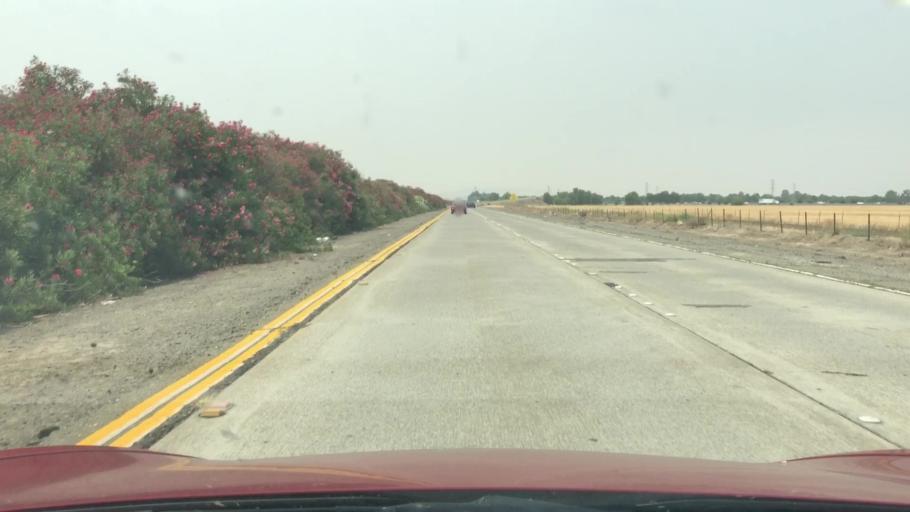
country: US
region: California
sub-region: San Joaquin County
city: Tracy
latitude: 37.7396
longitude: -121.4852
